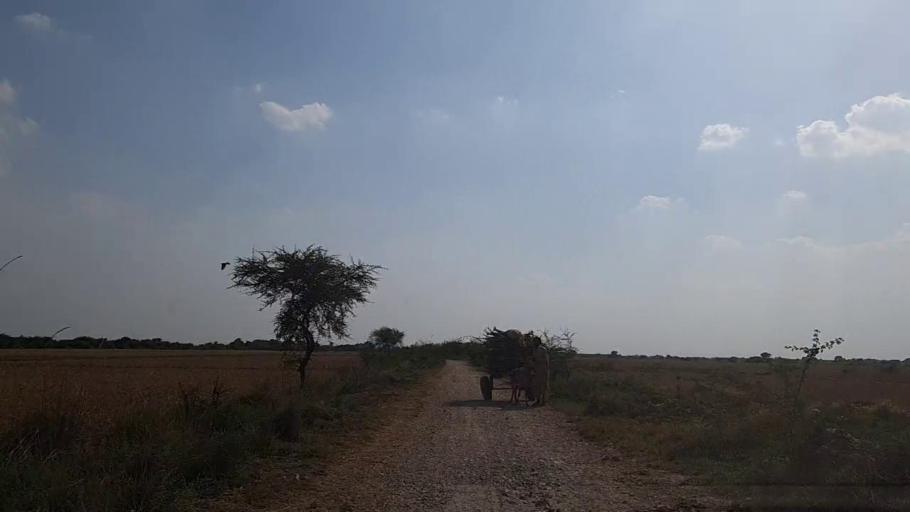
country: PK
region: Sindh
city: Jati
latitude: 24.4831
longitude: 68.3412
